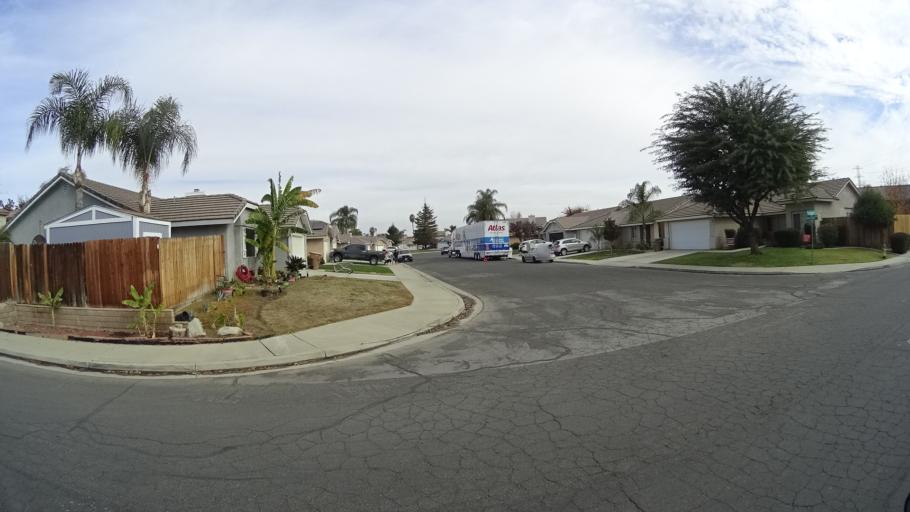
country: US
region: California
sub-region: Kern County
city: Rosedale
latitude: 35.3877
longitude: -119.1313
